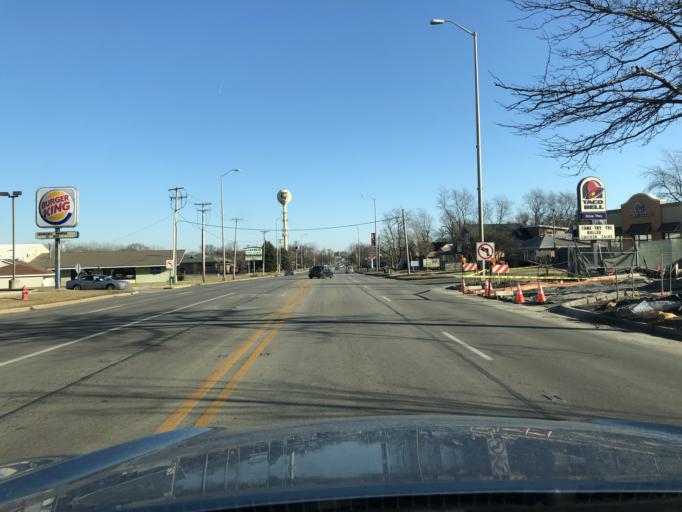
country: US
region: Illinois
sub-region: DuPage County
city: Wood Dale
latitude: 41.9653
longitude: -87.9896
